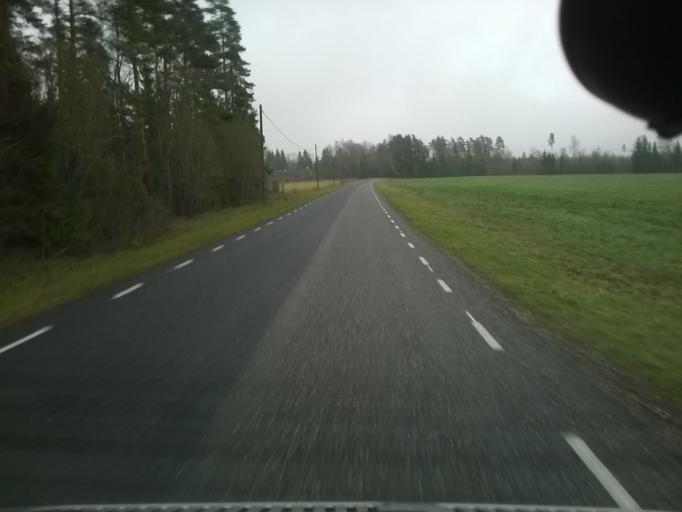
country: EE
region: Harju
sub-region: Saue linn
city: Saue
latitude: 59.1437
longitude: 24.5560
